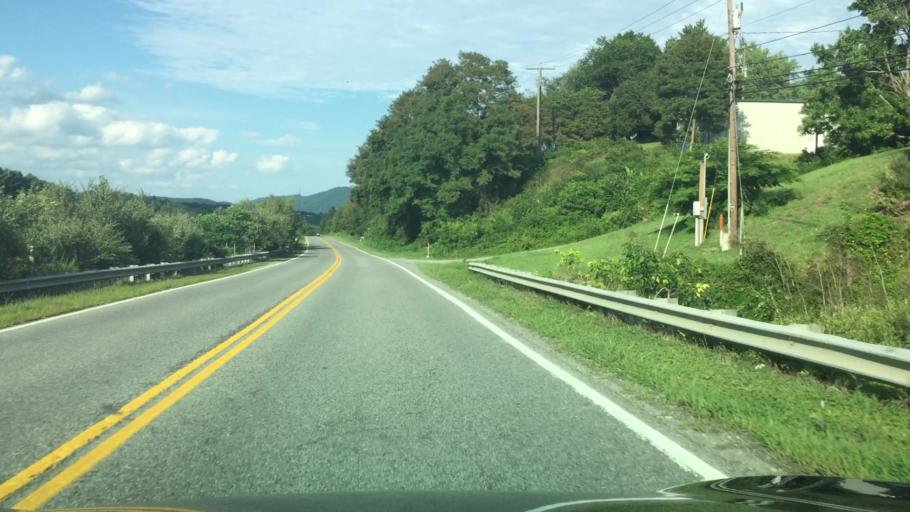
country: US
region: Virginia
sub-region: Wythe County
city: Wytheville
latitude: 36.9378
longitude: -80.9816
